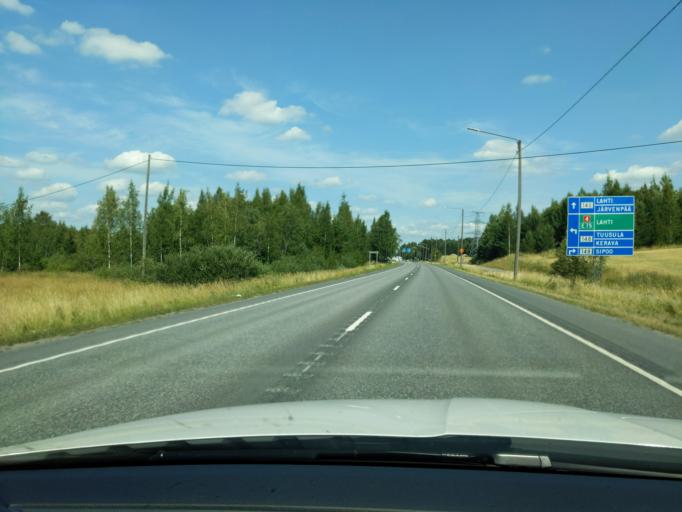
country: FI
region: Uusimaa
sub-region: Helsinki
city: Kerava
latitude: 60.3821
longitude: 25.1269
